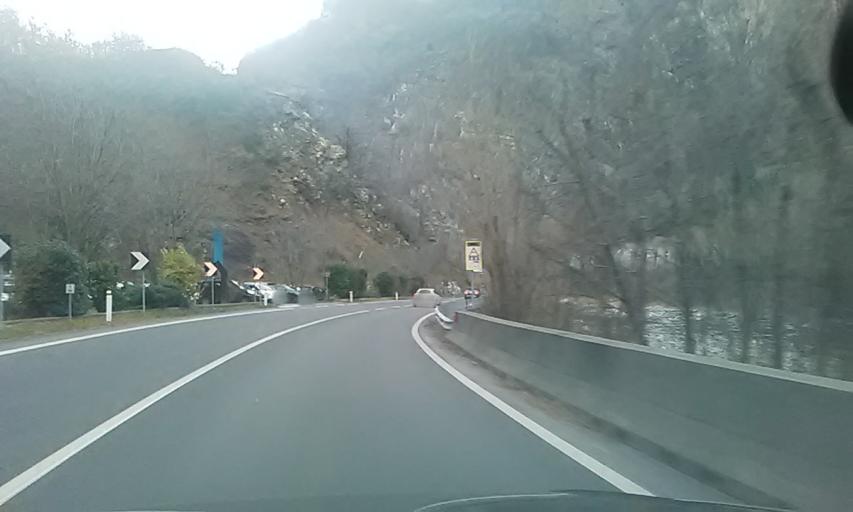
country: IT
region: Aosta Valley
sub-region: Valle d'Aosta
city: Bard
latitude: 45.6066
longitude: 7.7439
